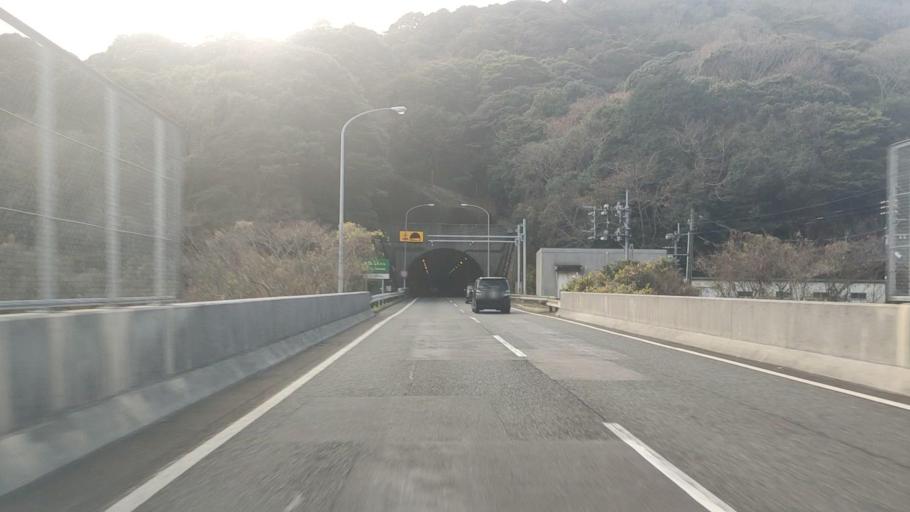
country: JP
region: Yamaguchi
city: Shimonoseki
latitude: 33.9210
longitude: 130.9691
